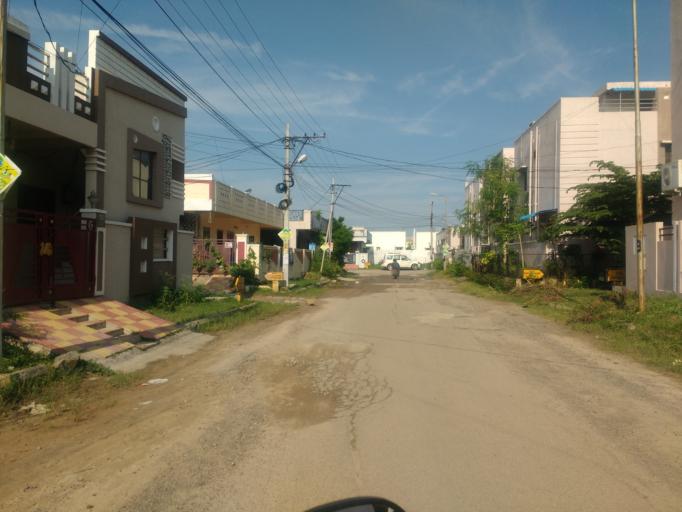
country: IN
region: Telangana
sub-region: Medak
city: Patancheru
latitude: 17.5329
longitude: 78.3023
